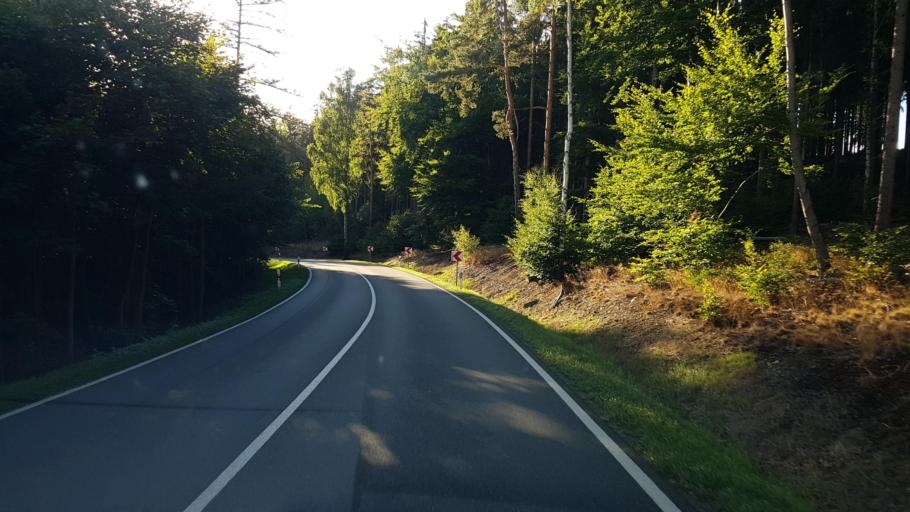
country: DE
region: Thuringia
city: Birkenhugel
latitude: 50.4455
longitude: 11.7190
